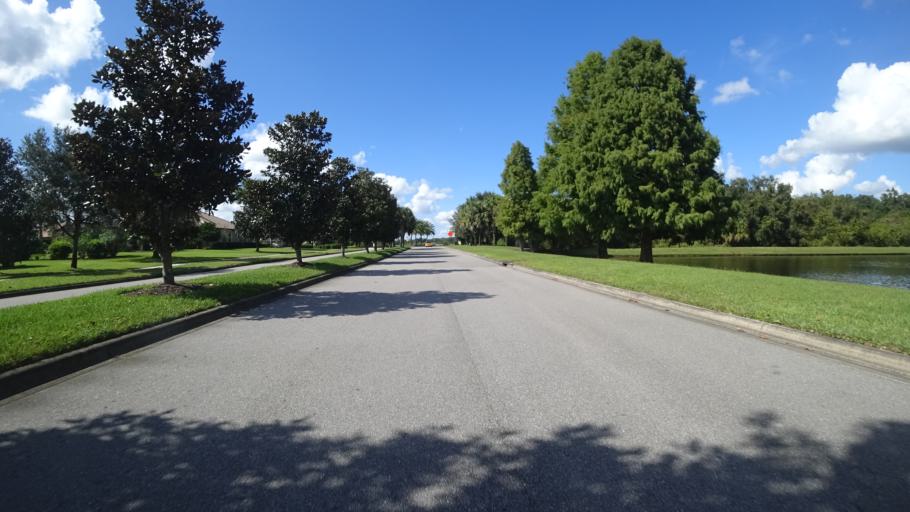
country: US
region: Florida
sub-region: Manatee County
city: Ellenton
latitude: 27.5042
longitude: -82.3729
